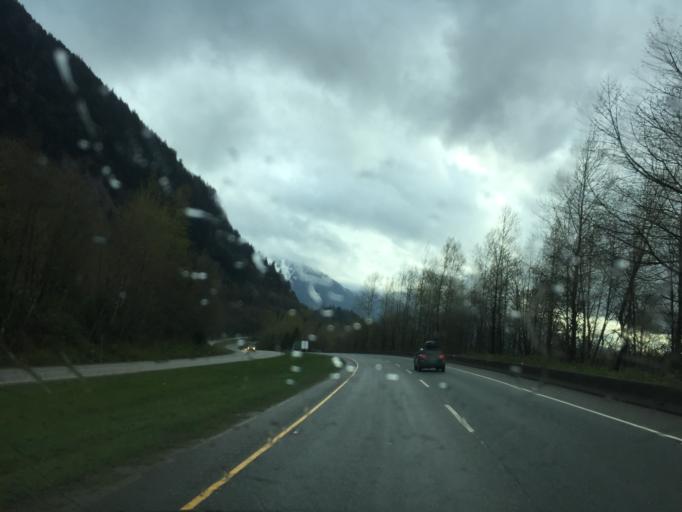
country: CA
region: British Columbia
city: Agassiz
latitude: 49.2822
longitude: -121.6709
